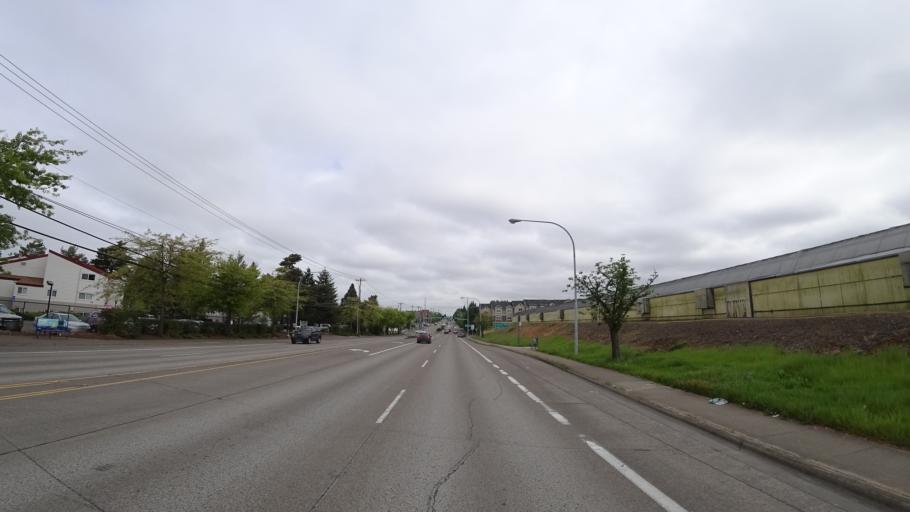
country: US
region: Oregon
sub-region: Washington County
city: Aloha
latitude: 45.5129
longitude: -122.8674
